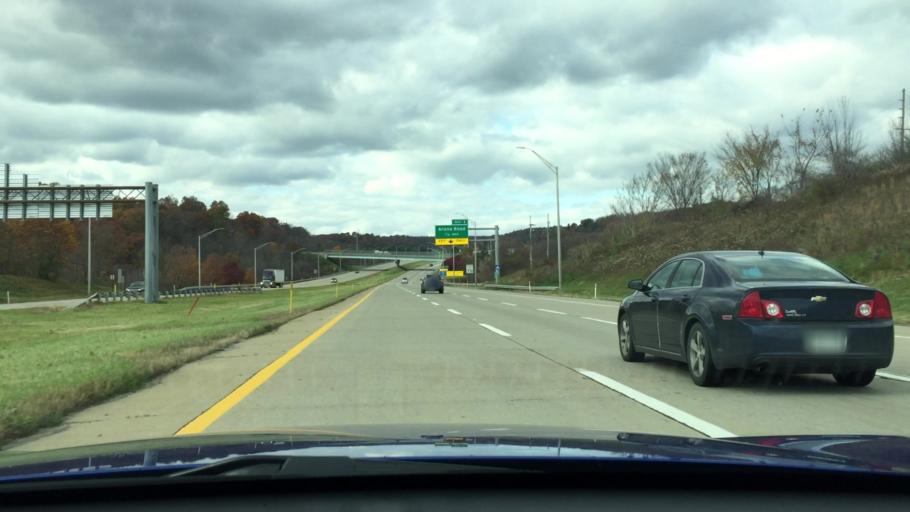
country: US
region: Pennsylvania
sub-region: Westmoreland County
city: New Stanton
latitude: 40.2291
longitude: -79.5973
